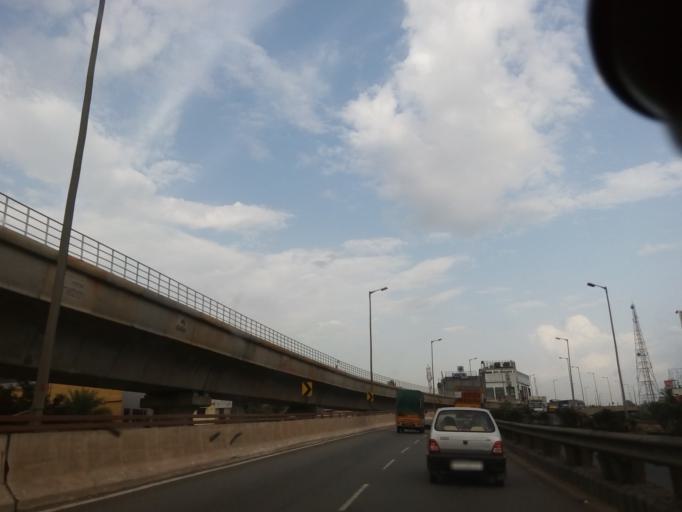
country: IN
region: Karnataka
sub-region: Bangalore Urban
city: Yelahanka
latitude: 13.0420
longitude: 77.5157
